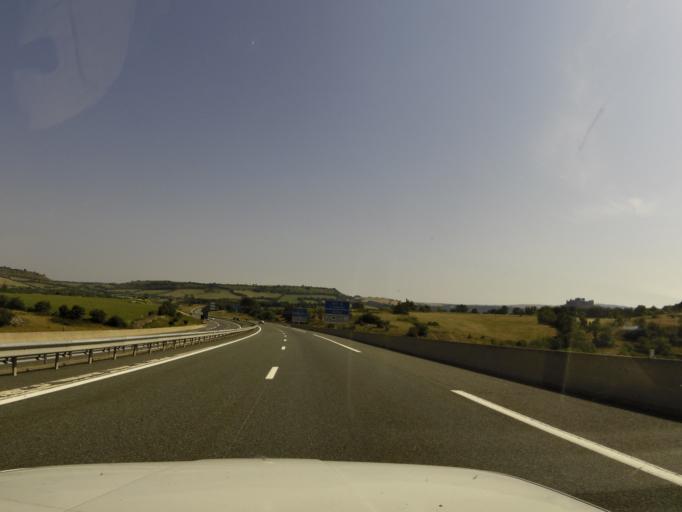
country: FR
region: Midi-Pyrenees
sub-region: Departement de l'Aveyron
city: Severac-le-Chateau
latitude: 44.3388
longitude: 3.0827
